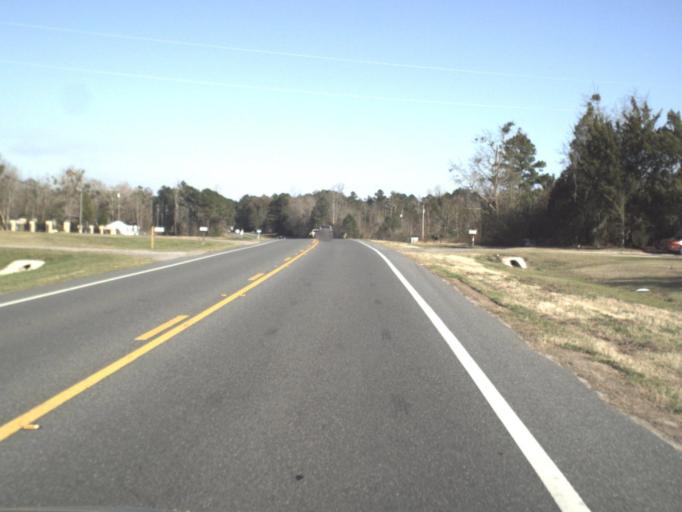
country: US
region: Florida
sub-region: Jackson County
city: Marianna
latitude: 30.7400
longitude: -85.1429
